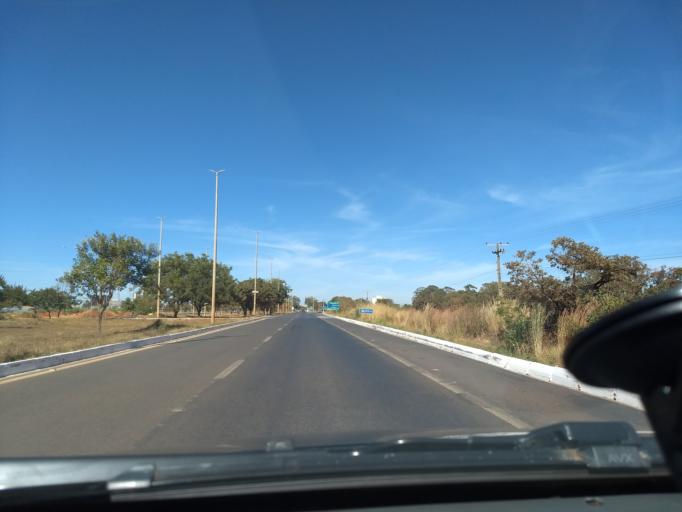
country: BR
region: Federal District
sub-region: Brasilia
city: Brasilia
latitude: -15.7881
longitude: -48.0518
